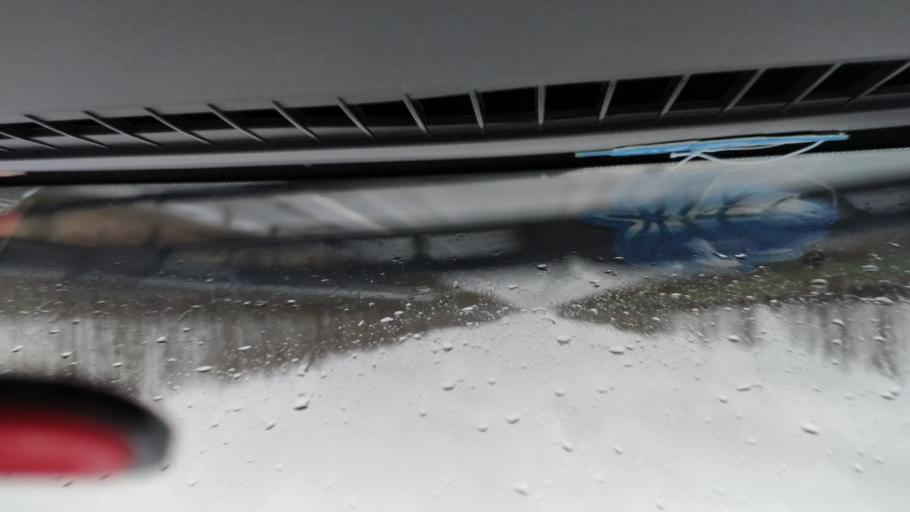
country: RU
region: Tatarstan
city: Mendeleyevsk
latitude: 55.9337
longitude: 52.2845
